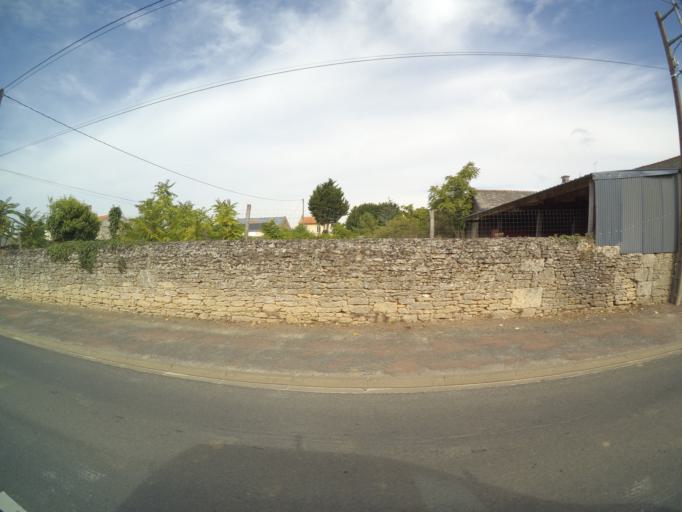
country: FR
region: Pays de la Loire
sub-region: Departement de Maine-et-Loire
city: Doue-la-Fontaine
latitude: 47.1930
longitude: -0.2908
